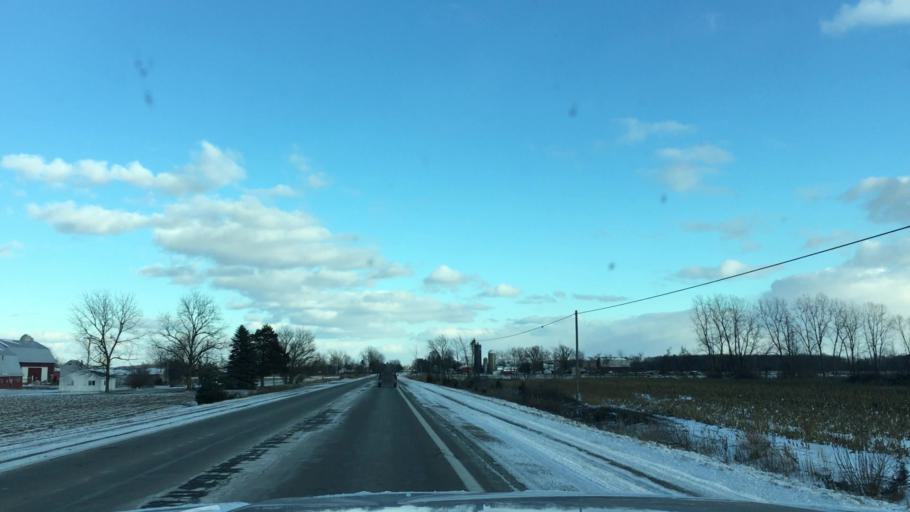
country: US
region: Michigan
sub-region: Saginaw County
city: Chesaning
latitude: 43.1869
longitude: -84.1964
